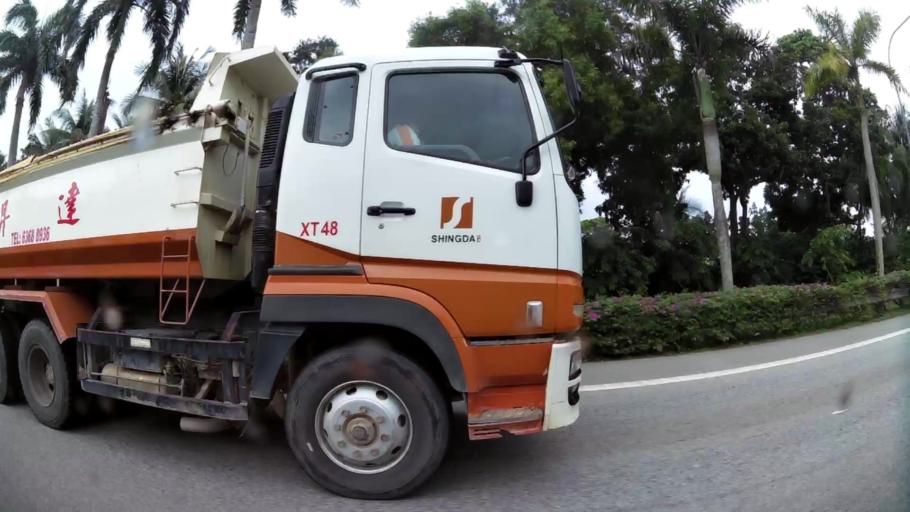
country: SG
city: Singapore
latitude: 1.3179
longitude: 103.9651
